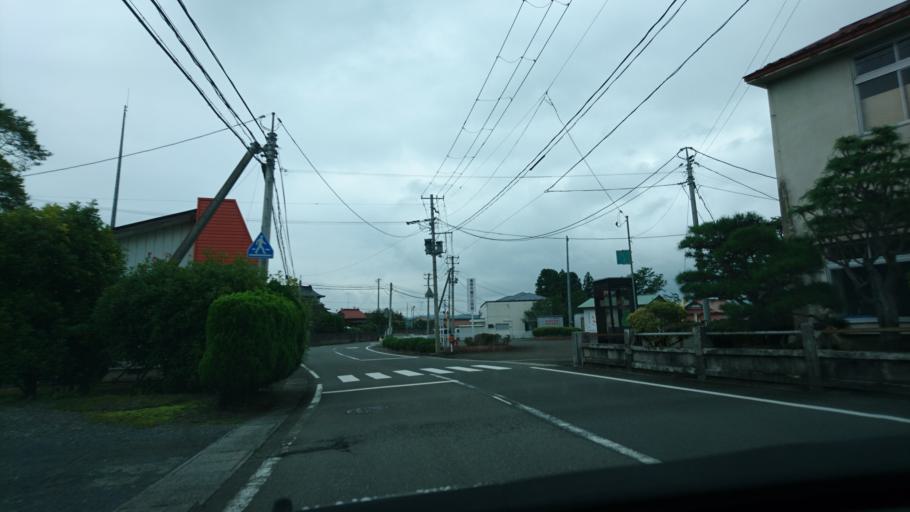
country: JP
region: Iwate
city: Ichinoseki
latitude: 38.8064
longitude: 140.9437
